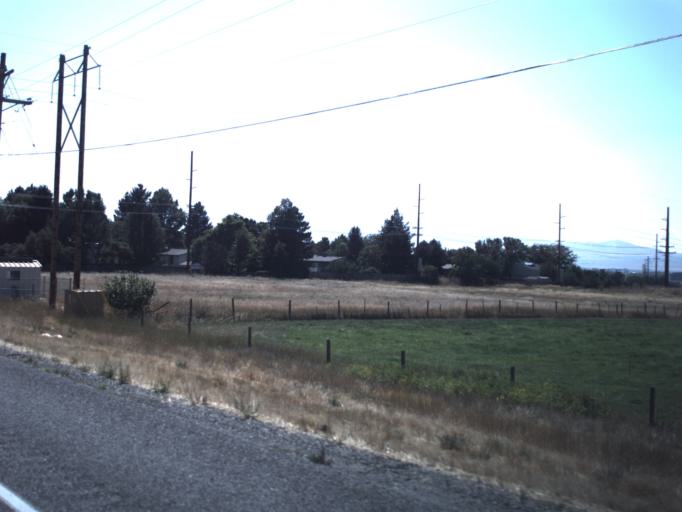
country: US
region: Utah
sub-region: Cache County
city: Smithfield
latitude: 41.8535
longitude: -111.8319
